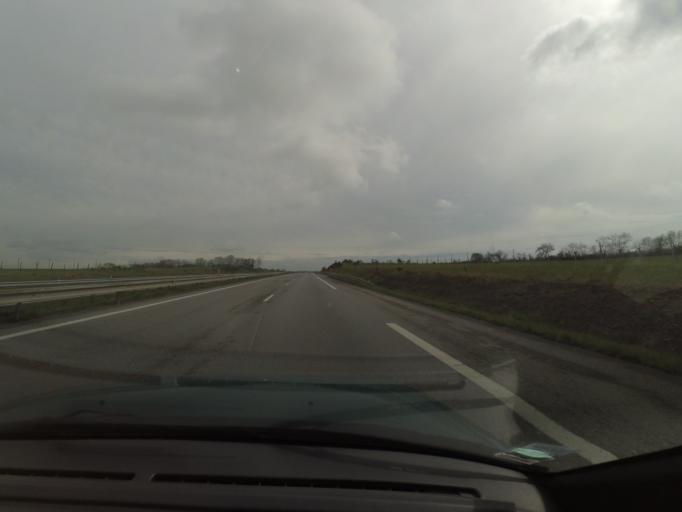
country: FR
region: Pays de la Loire
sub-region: Departement de la Loire-Atlantique
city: Ancenis
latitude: 47.4119
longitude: -1.1498
